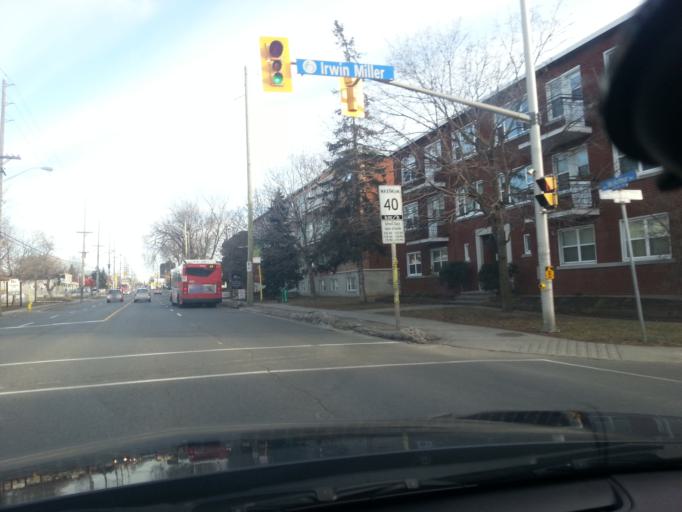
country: CA
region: Ontario
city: Ottawa
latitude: 45.4318
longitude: -75.6529
